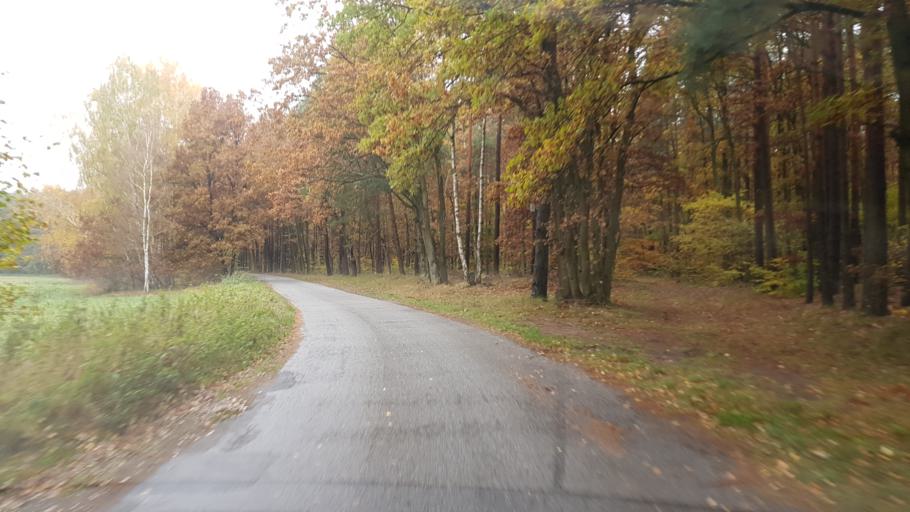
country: PL
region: West Pomeranian Voivodeship
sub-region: Powiat gryfinski
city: Chojna
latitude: 53.0550
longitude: 14.5024
